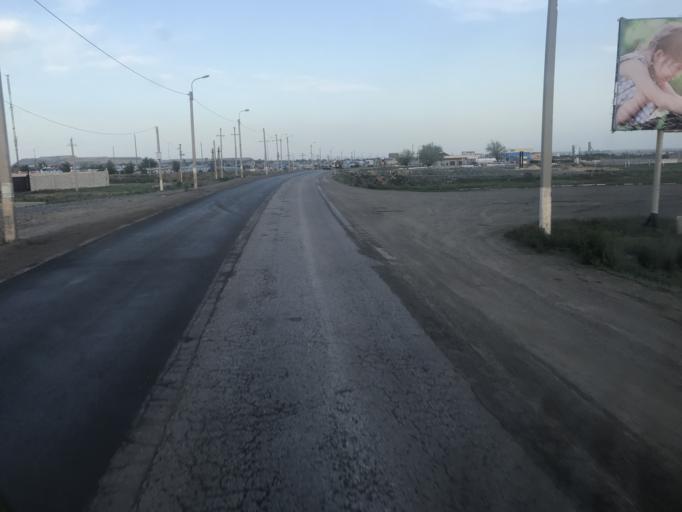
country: KZ
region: Aqtoebe
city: Khromtau
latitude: 50.2582
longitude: 58.4104
